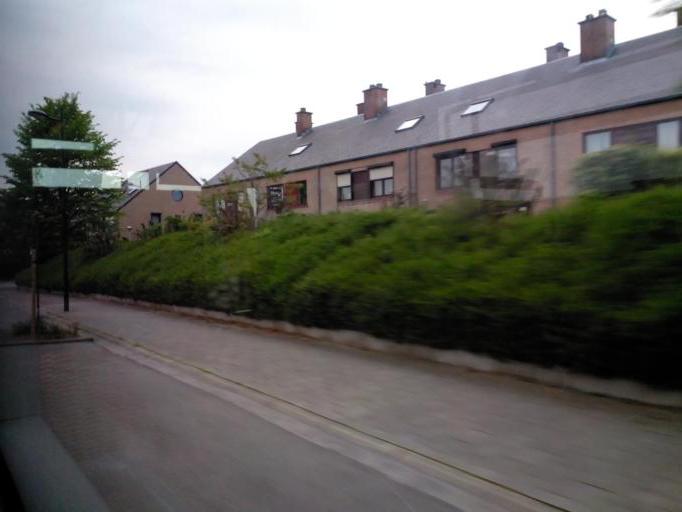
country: BE
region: Flanders
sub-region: Provincie Vlaams-Brabant
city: Diegem
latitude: 50.8584
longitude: 4.4072
